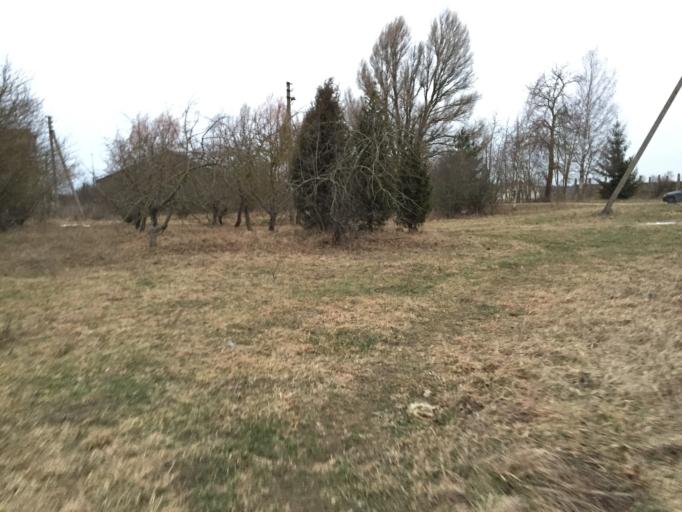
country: LT
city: Zagare
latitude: 56.3380
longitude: 23.2691
